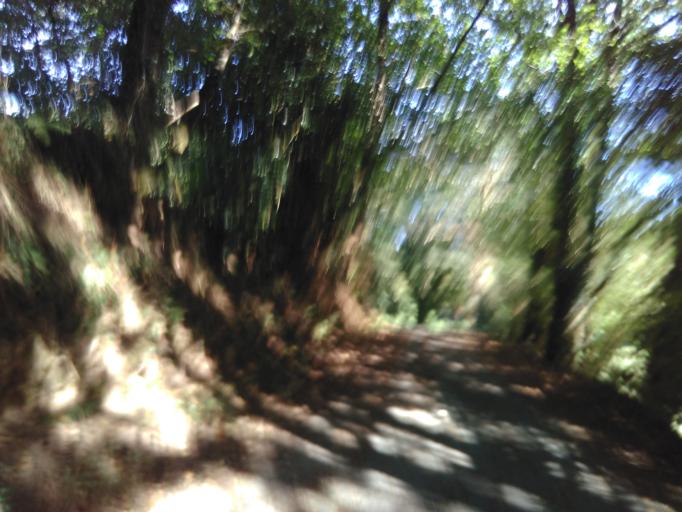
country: FR
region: Pays de la Loire
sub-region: Departement de la Vendee
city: La Chaize-le-Vicomte
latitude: 46.6622
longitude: -1.3043
